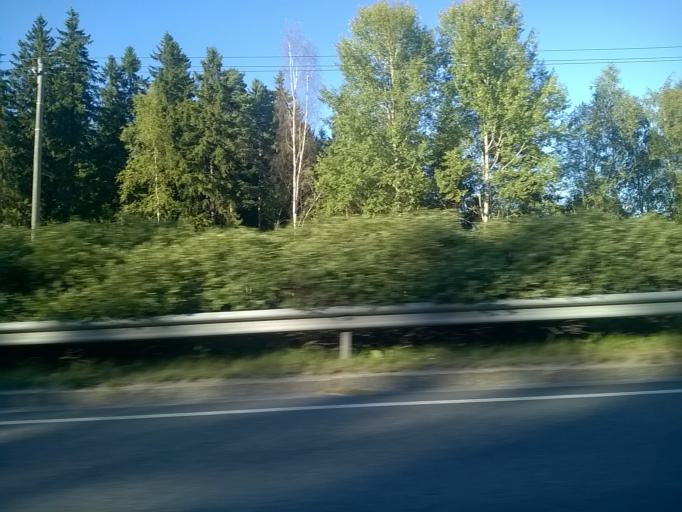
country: FI
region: Pirkanmaa
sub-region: Tampere
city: Tampere
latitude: 61.5004
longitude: 23.8748
